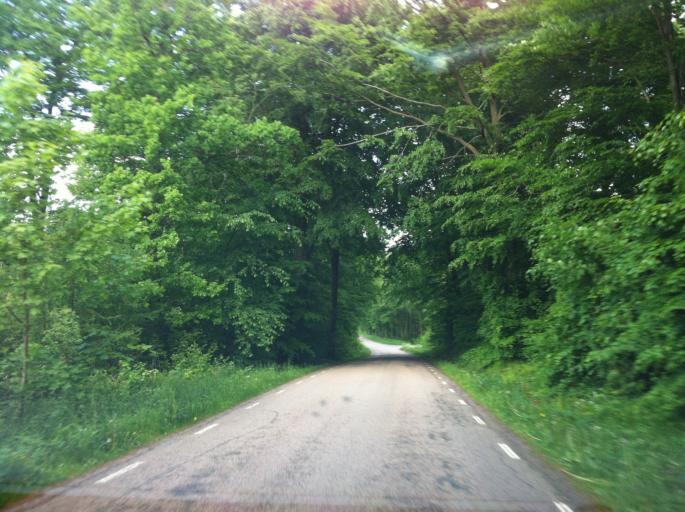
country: SE
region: Skane
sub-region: Svalovs Kommun
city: Svaloev
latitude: 55.9565
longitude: 13.0389
